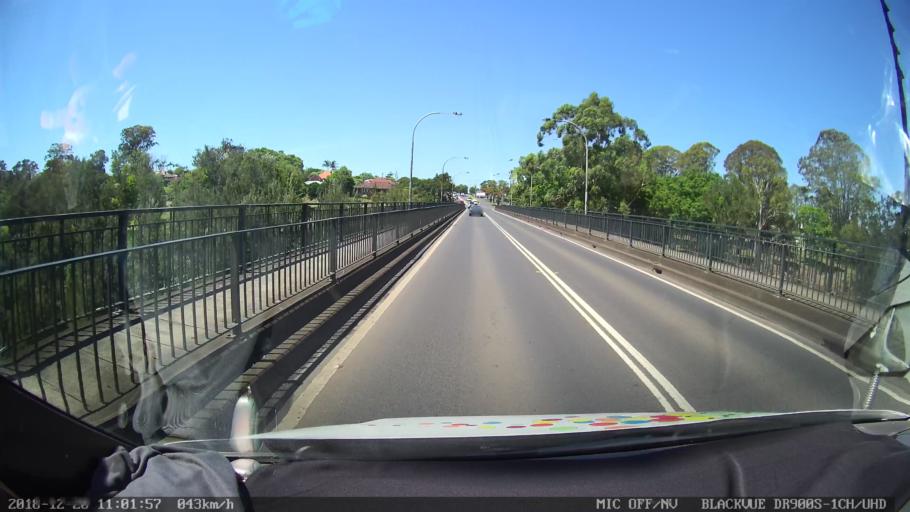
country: AU
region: New South Wales
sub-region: Richmond Valley
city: Casino
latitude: -28.8681
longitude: 153.0448
